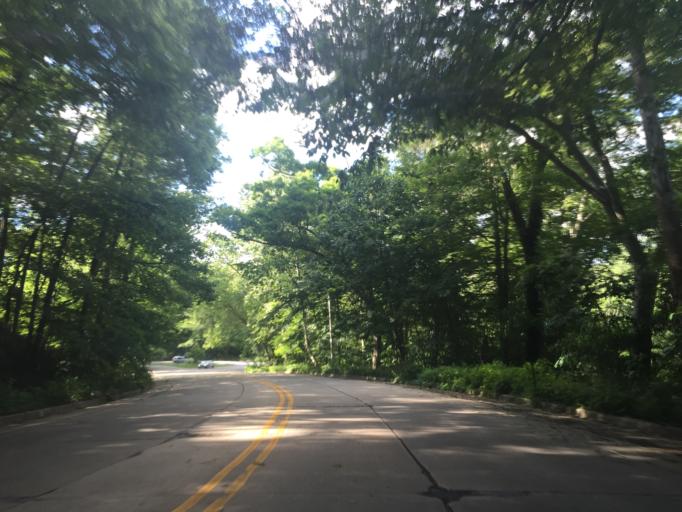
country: US
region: Maryland
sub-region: Baltimore County
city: Pikesville
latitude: 39.3653
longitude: -76.6642
